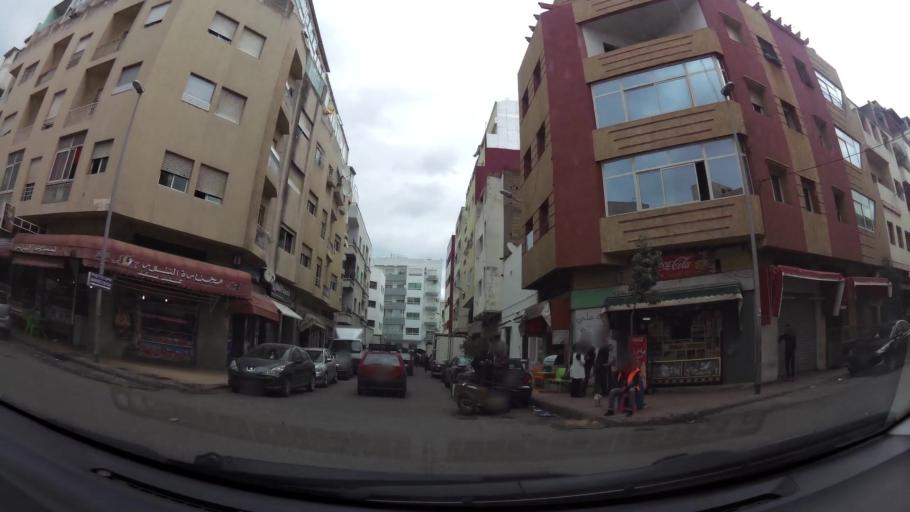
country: MA
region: Grand Casablanca
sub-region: Casablanca
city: Casablanca
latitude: 33.5696
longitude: -7.6476
